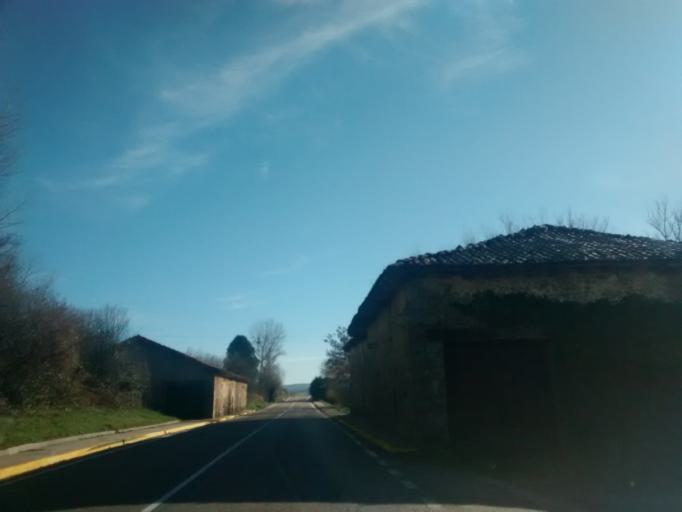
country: ES
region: Castille and Leon
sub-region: Provincia de Burgos
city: Arija
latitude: 42.9822
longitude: -3.8131
